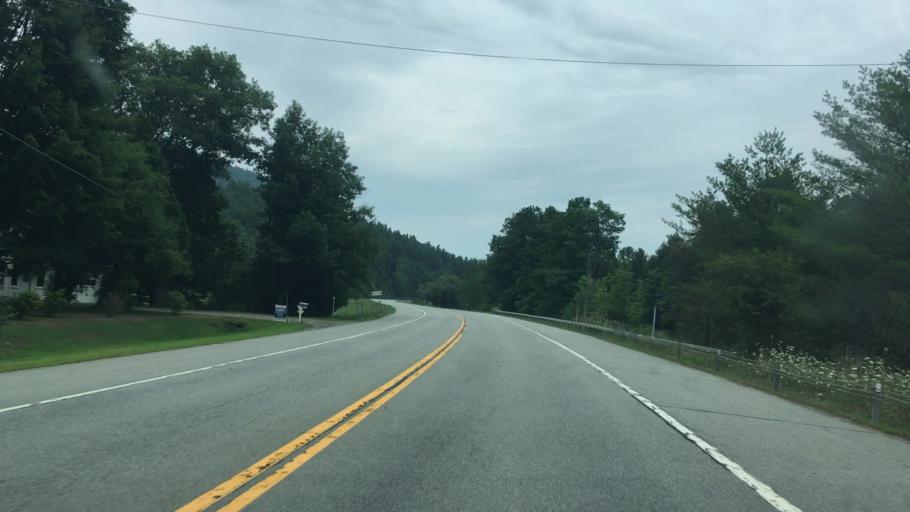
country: US
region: New York
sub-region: Essex County
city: Elizabethtown
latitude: 44.3492
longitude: -73.7572
